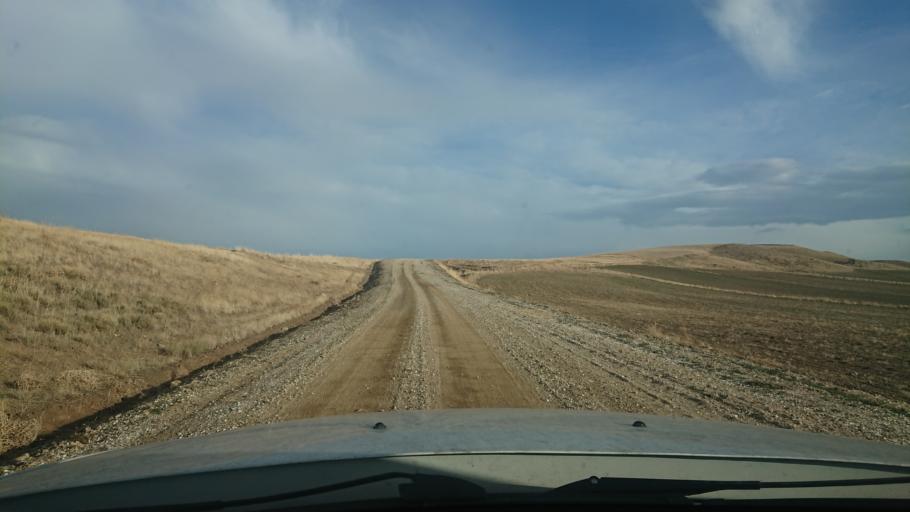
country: TR
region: Aksaray
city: Acipinar
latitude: 38.6875
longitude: 33.8697
